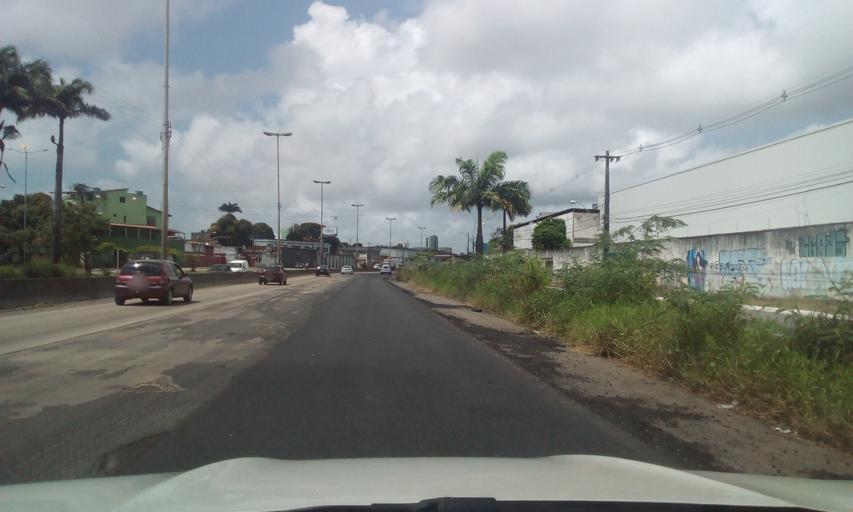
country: BR
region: Pernambuco
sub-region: Recife
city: Recife
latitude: -8.0342
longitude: -34.9419
